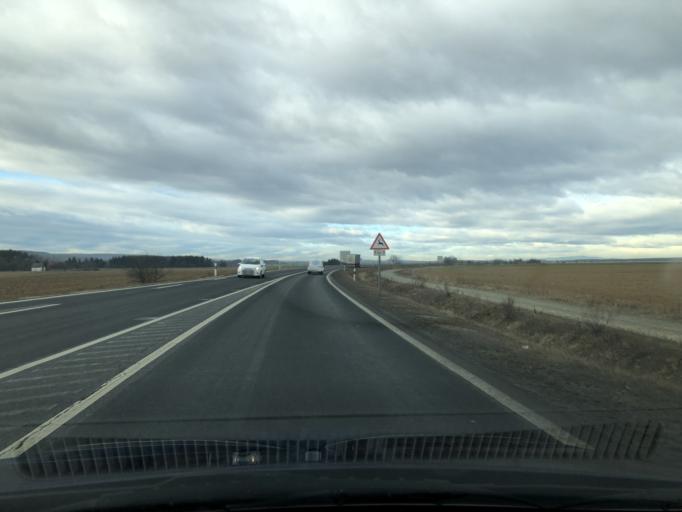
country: HU
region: Vas
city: Gencsapati
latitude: 47.2490
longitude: 16.5673
